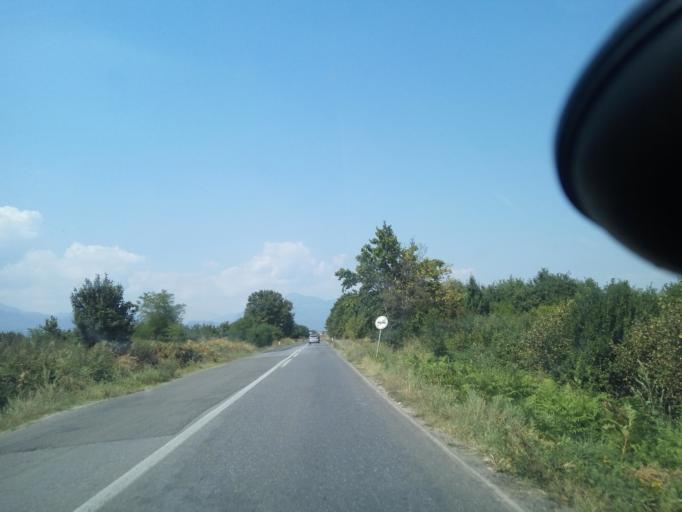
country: XK
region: Gjakova
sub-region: Komuna e Decanit
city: Gllogjan
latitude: 42.4390
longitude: 20.3692
